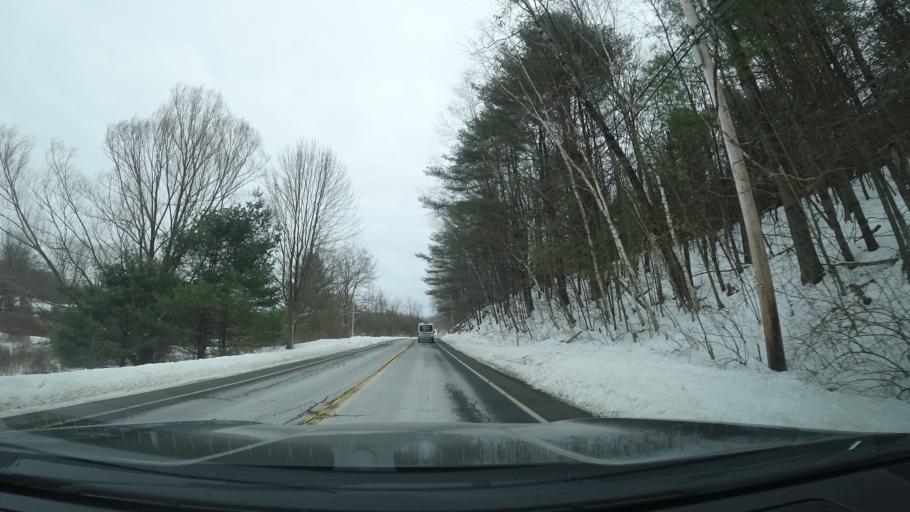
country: US
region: New York
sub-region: Washington County
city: Greenwich
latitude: 43.1867
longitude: -73.4715
